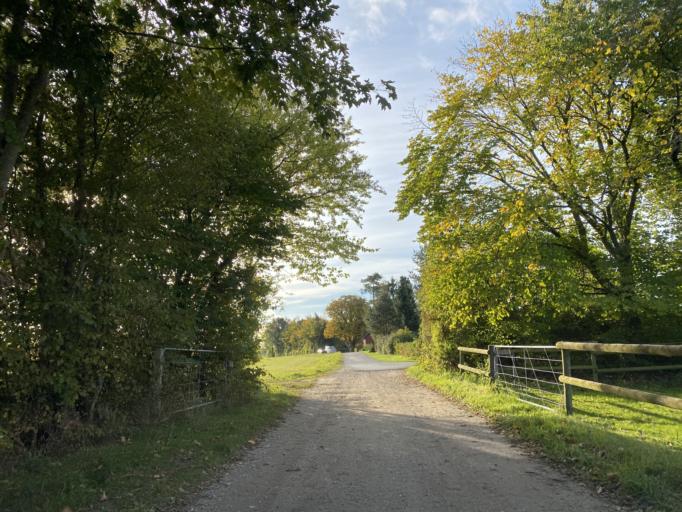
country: DK
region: Capital Region
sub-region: Allerod Kommune
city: Lynge
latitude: 55.8173
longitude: 12.2836
